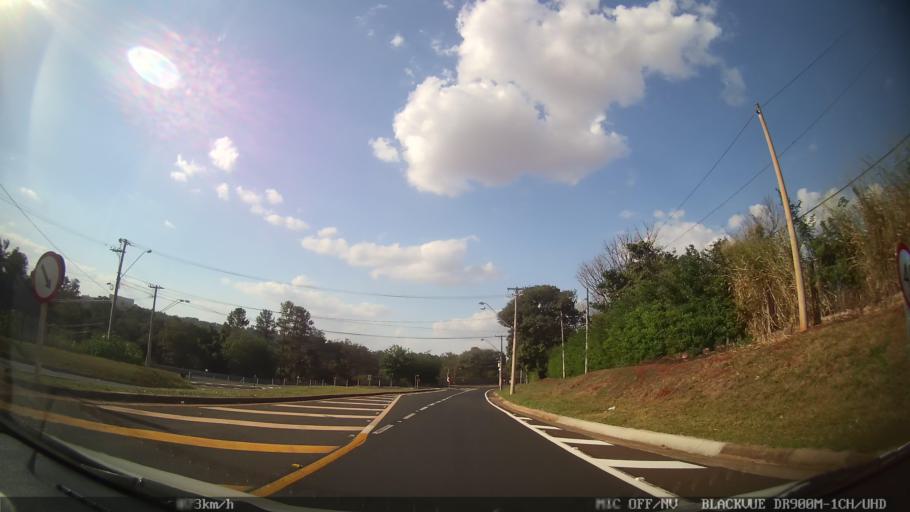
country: BR
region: Sao Paulo
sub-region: Ribeirao Preto
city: Ribeirao Preto
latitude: -21.1773
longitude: -47.8536
